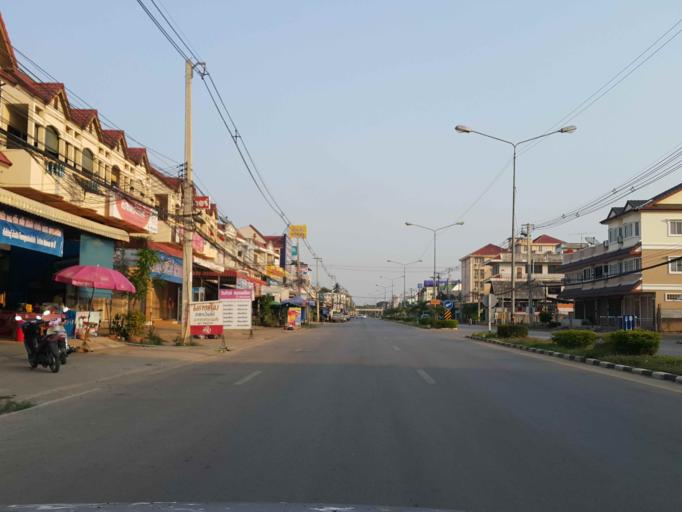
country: TH
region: Sukhothai
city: Sawankhalok
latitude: 17.3014
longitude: 99.8345
